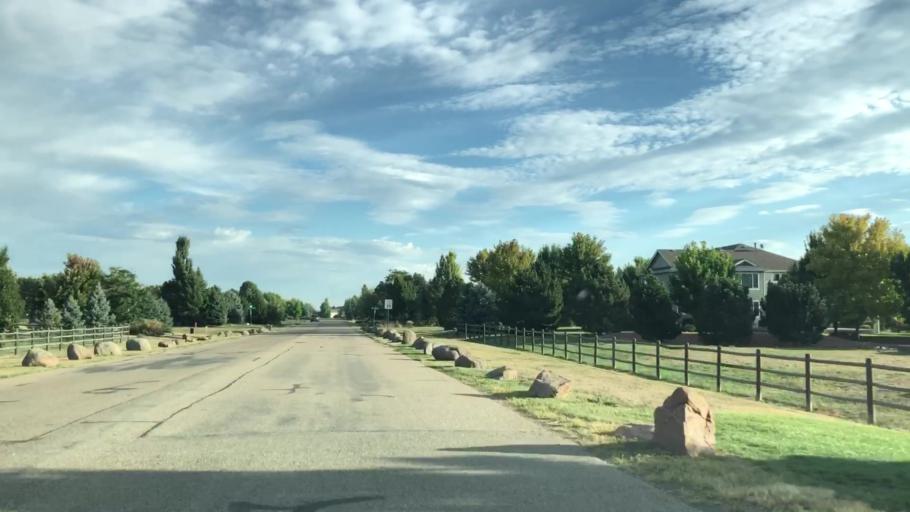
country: US
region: Colorado
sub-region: Weld County
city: Windsor
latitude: 40.4363
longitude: -104.9513
